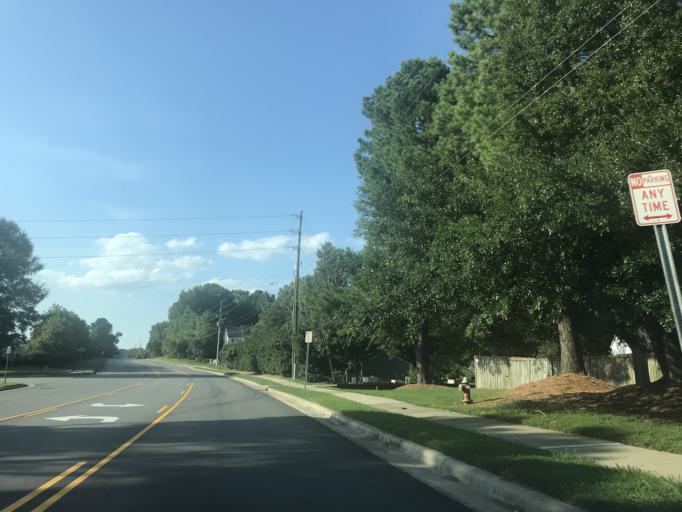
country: US
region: North Carolina
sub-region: Wake County
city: Knightdale
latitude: 35.7833
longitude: -78.5453
